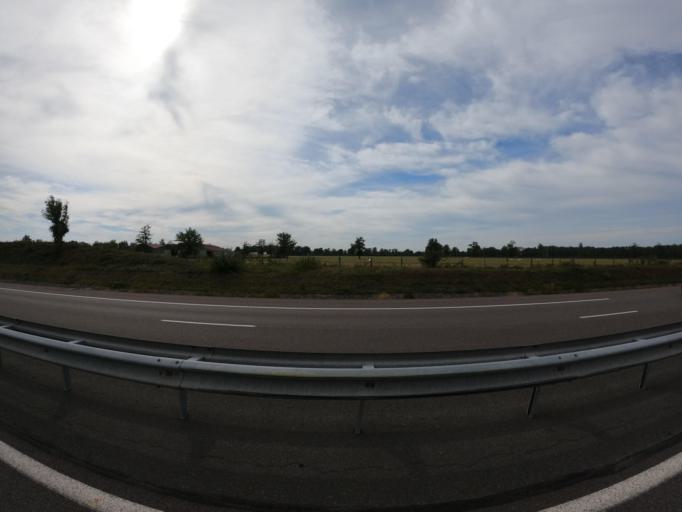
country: FR
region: Bourgogne
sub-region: Departement de Saone-et-Loire
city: Saint-Yan
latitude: 46.4667
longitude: 4.0463
